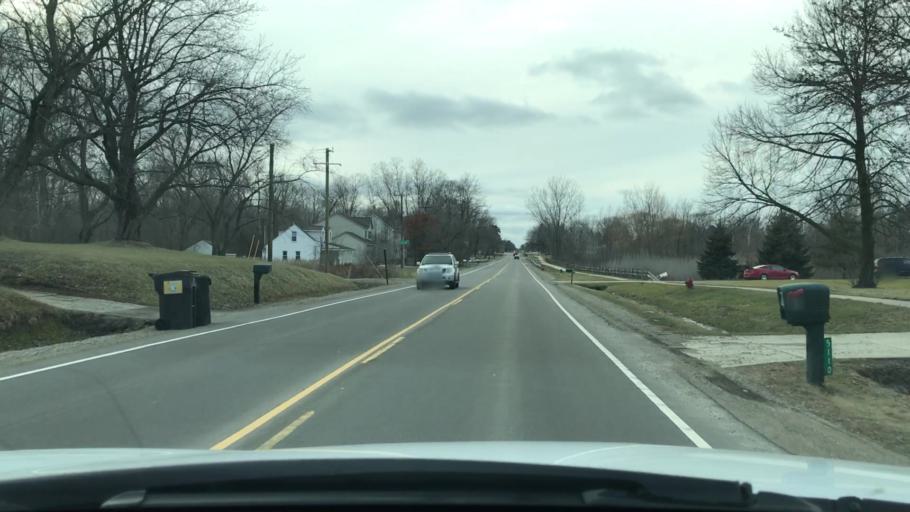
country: US
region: Michigan
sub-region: Oakland County
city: Waterford
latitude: 42.7199
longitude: -83.3510
